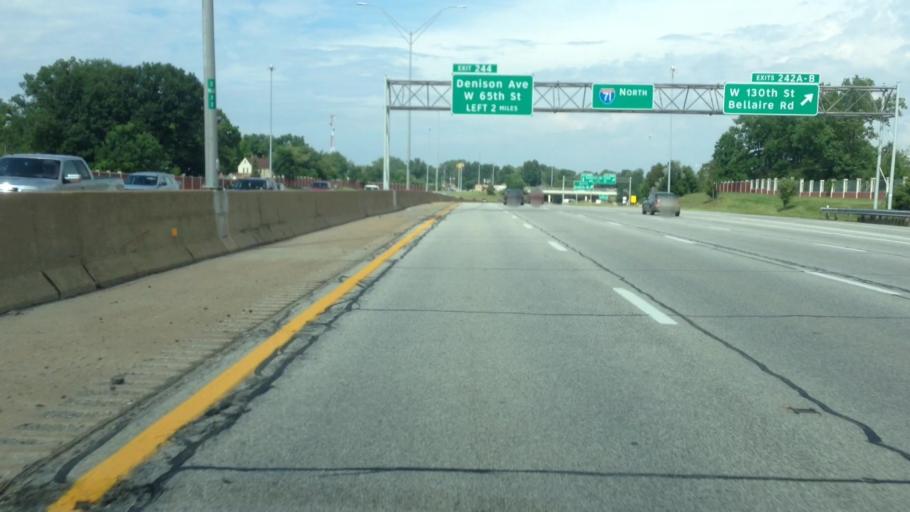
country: US
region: Ohio
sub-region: Cuyahoga County
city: Lakewood
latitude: 41.4425
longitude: -81.7849
